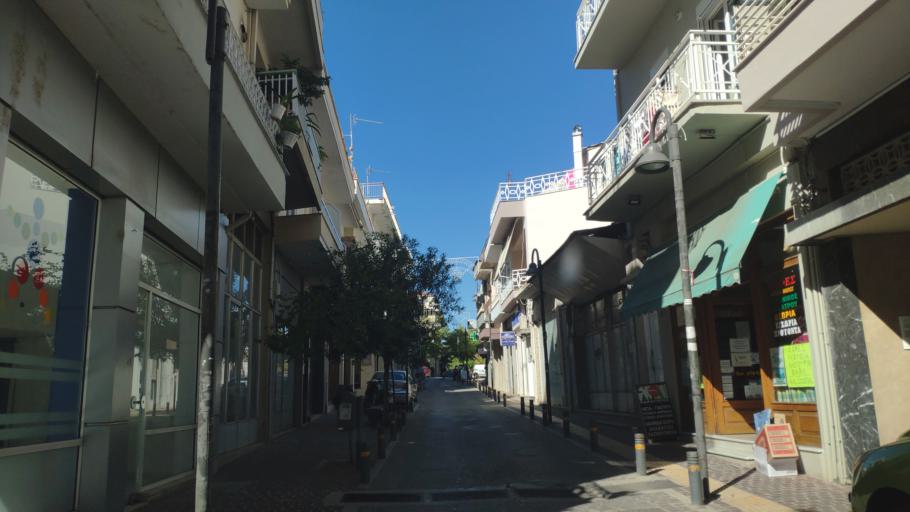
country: GR
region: Central Greece
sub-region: Nomos Voiotias
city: Livadeia
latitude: 38.4374
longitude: 22.8736
